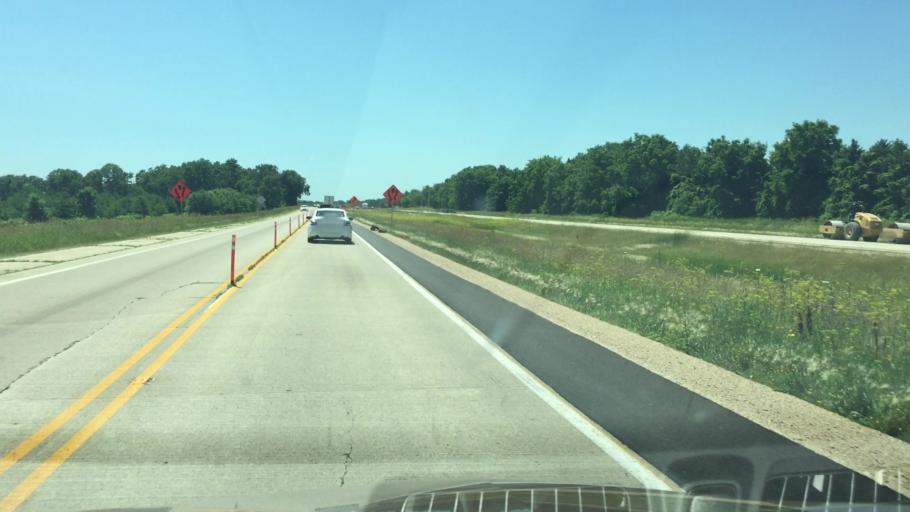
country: US
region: Wisconsin
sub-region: Dane County
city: Marshall
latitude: 43.2513
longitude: -89.1307
